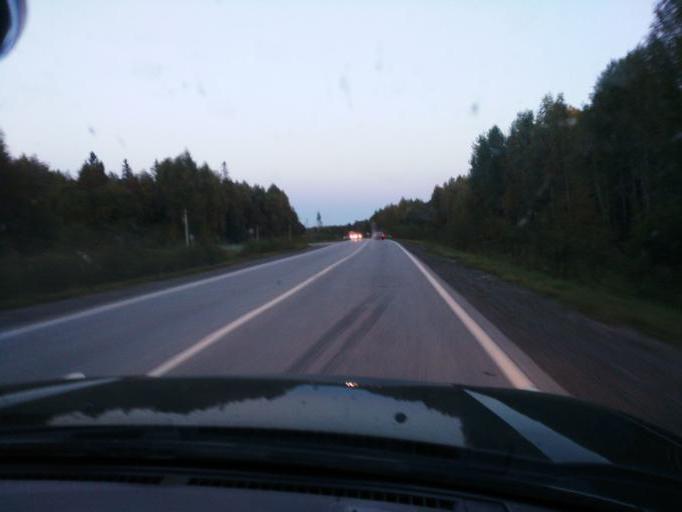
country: RU
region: Perm
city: Verkhnechusovskiye Gorodki
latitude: 58.2477
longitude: 57.0198
